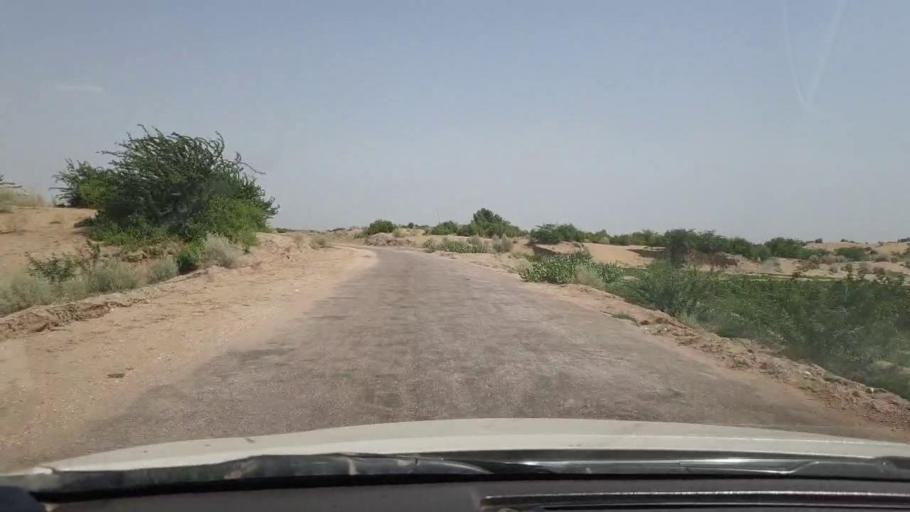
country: PK
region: Sindh
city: Rohri
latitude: 27.4960
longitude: 69.0440
